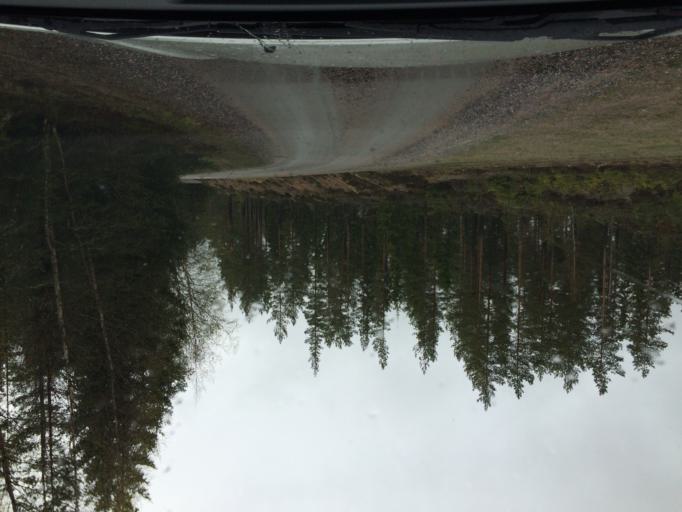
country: SE
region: OErebro
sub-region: Hallefors Kommun
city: Haellefors
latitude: 60.0159
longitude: 14.5872
